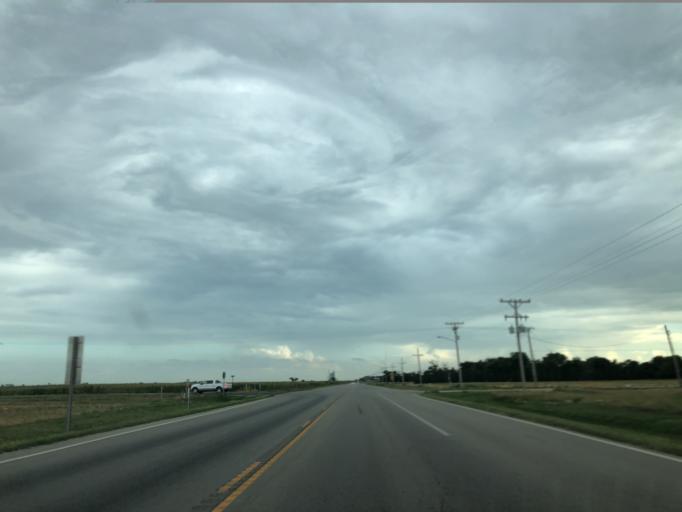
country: US
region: Kansas
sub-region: Rice County
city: Lyons
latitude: 38.2908
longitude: -98.2020
